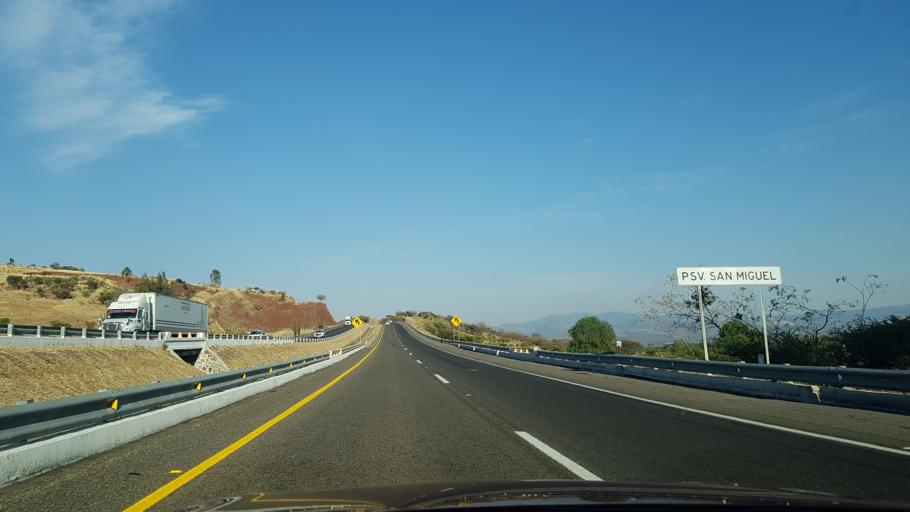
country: MX
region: Michoacan
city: Maravatio
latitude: 19.9071
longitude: -100.5028
